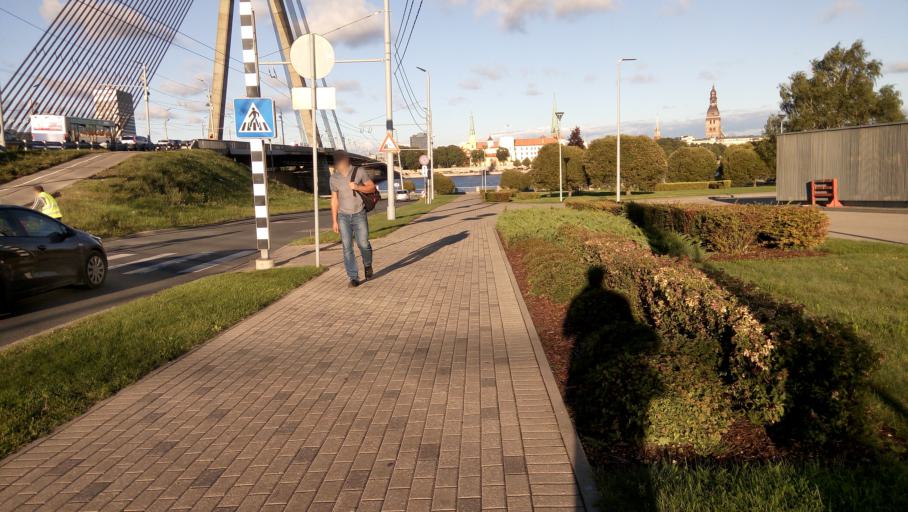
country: LV
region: Riga
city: Riga
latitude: 56.9493
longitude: 24.0892
